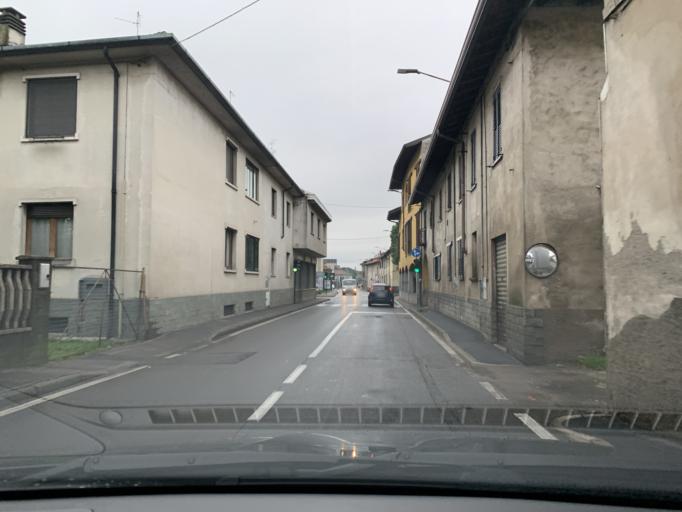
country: IT
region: Lombardy
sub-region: Provincia di Como
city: Rovello Porro
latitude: 45.6385
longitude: 9.0469
